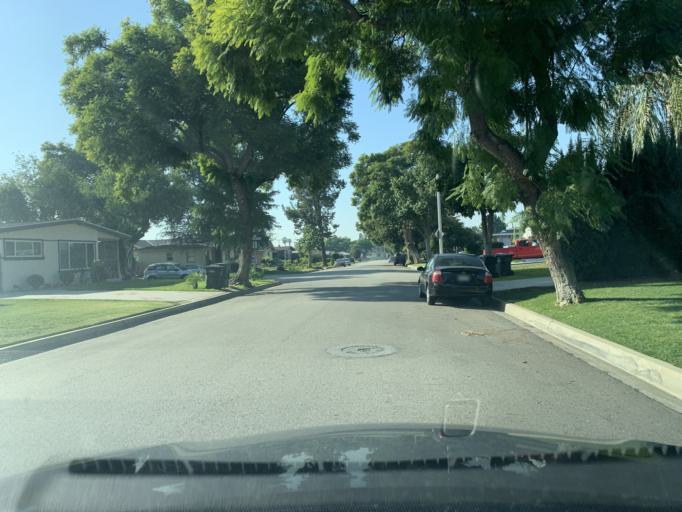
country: US
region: California
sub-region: Los Angeles County
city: Covina
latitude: 34.0732
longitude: -117.8935
